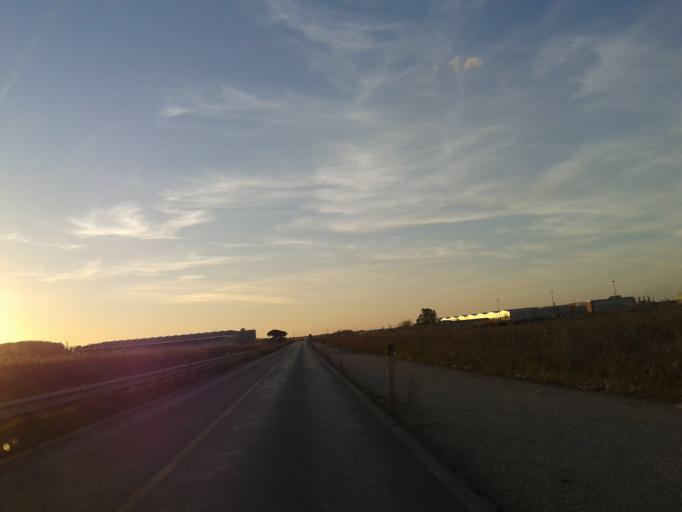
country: IT
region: Tuscany
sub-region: Provincia di Livorno
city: Guasticce
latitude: 43.5968
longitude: 10.3875
